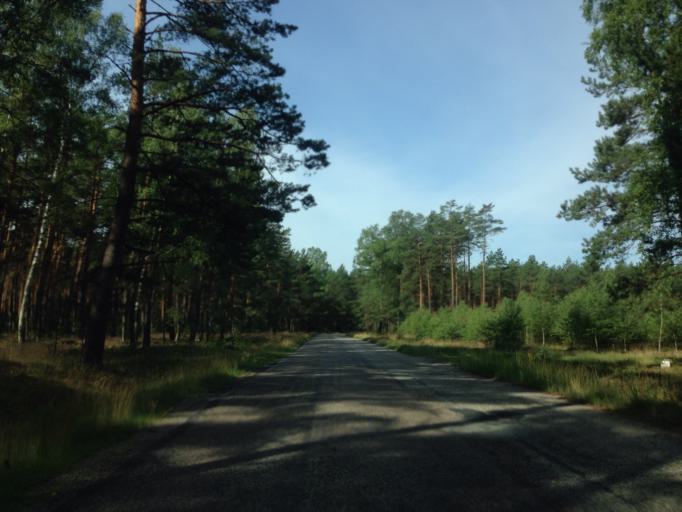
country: PL
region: Kujawsko-Pomorskie
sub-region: Powiat swiecki
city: Osie
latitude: 53.6980
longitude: 18.3251
